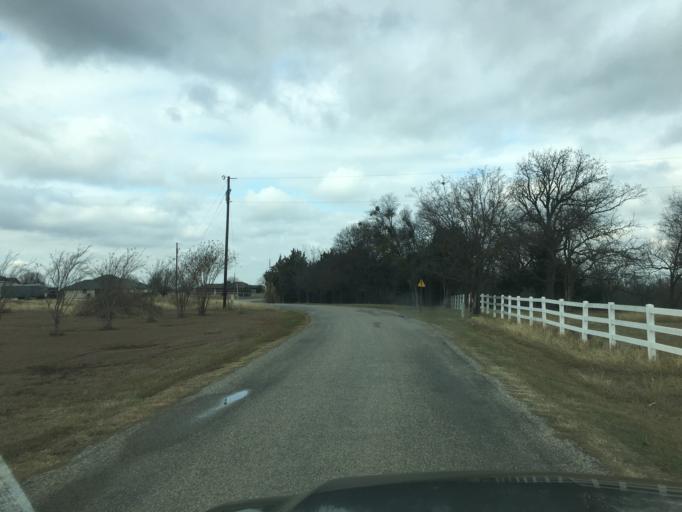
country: US
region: Texas
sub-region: Ellis County
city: Palmer
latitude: 32.4640
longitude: -96.6399
